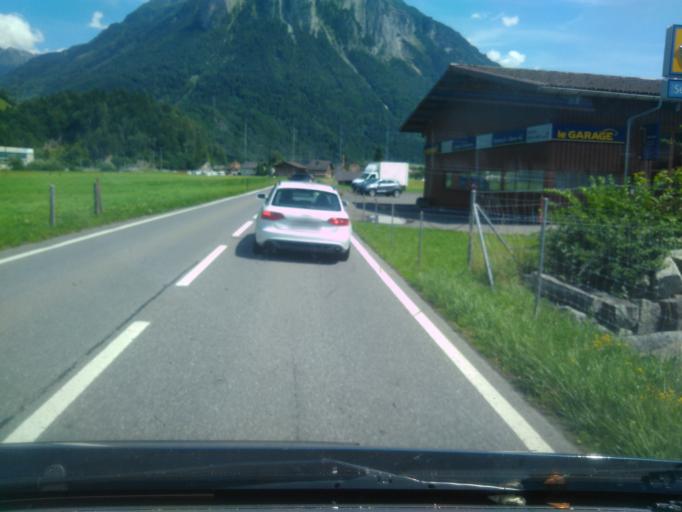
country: CH
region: Bern
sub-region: Interlaken-Oberhasli District
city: Meiringen
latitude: 46.7083
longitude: 8.2195
